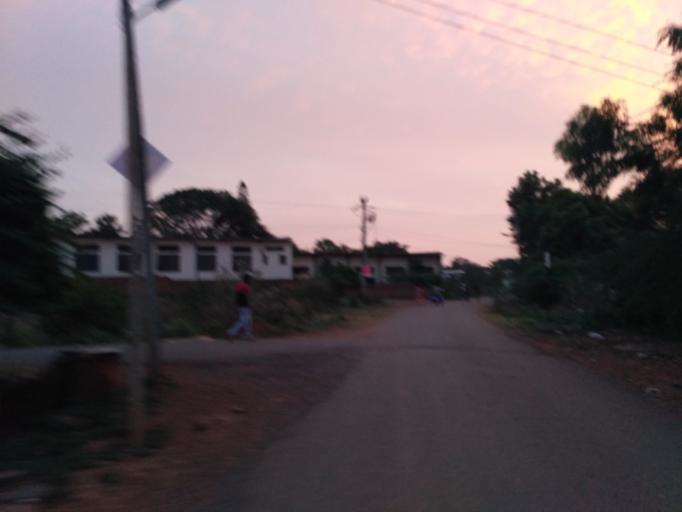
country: IN
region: Karnataka
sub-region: Dharwad
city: Hubli
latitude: 15.4428
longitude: 75.0185
